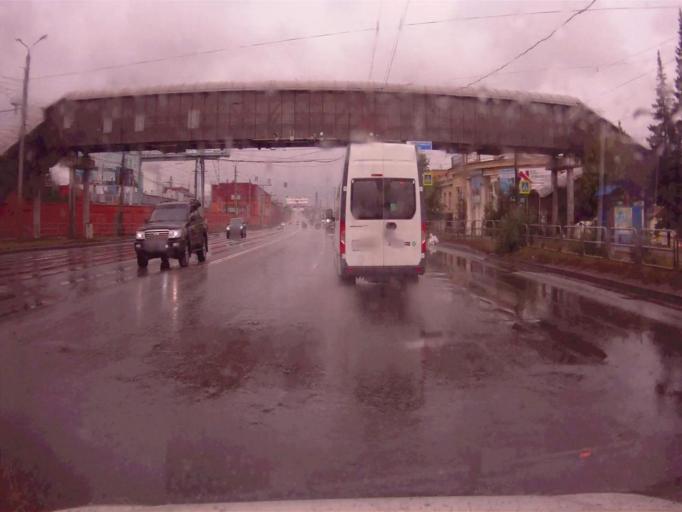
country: RU
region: Chelyabinsk
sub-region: Gorod Chelyabinsk
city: Chelyabinsk
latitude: 55.2052
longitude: 61.3850
